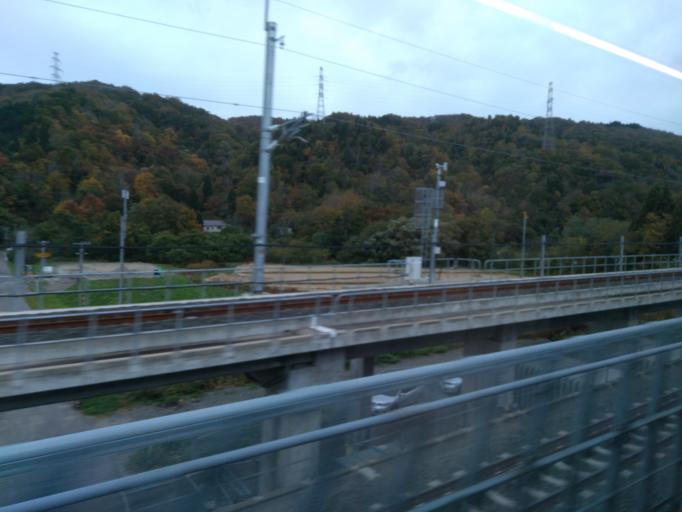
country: JP
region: Aomori
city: Goshogawara
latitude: 41.1479
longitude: 140.5132
